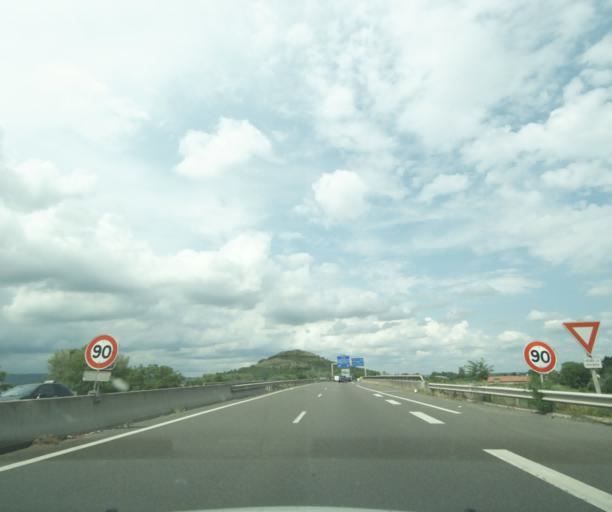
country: FR
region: Auvergne
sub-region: Departement du Puy-de-Dome
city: Perignat-les-Sarlieve
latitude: 45.7639
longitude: 3.1389
